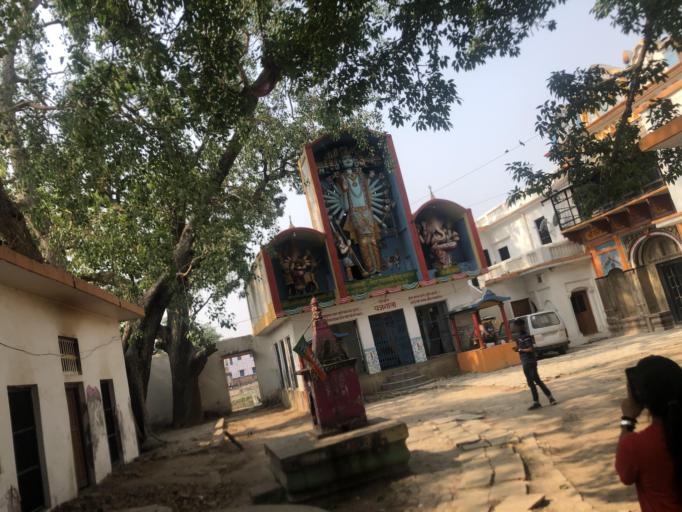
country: IN
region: Uttar Pradesh
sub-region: Faizabad
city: Ayodhya
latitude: 26.7837
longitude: 82.2030
